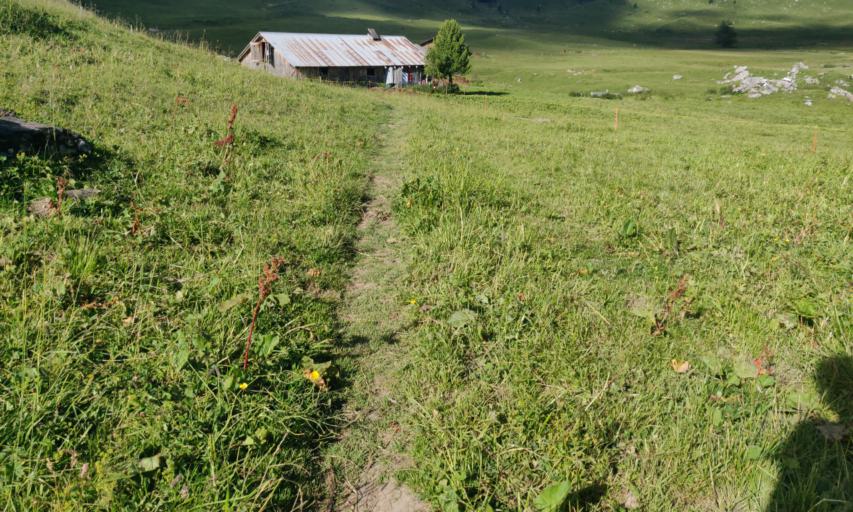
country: CH
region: Bern
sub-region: Obersimmental-Saanen District
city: Gstaad
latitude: 46.3872
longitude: 7.3485
